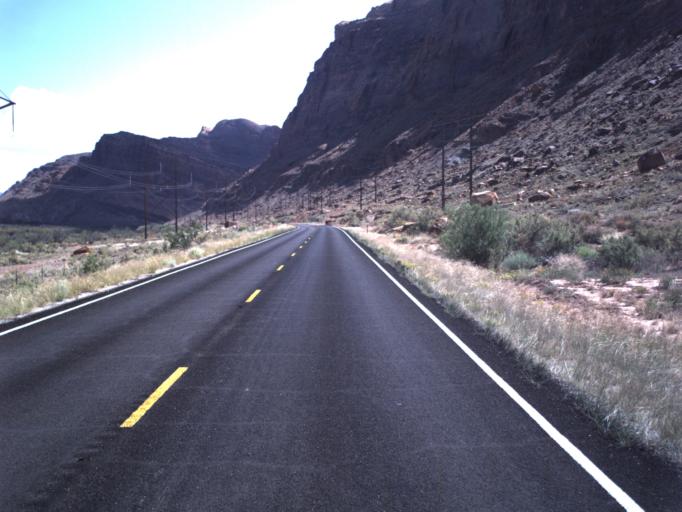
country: US
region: Utah
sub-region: Grand County
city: Moab
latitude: 38.5888
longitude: -109.5934
